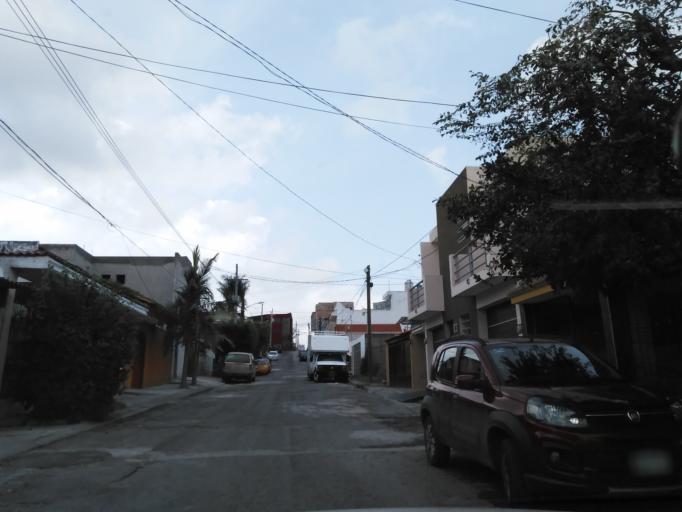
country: MX
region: Nayarit
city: Tepic
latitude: 21.5185
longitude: -104.9184
